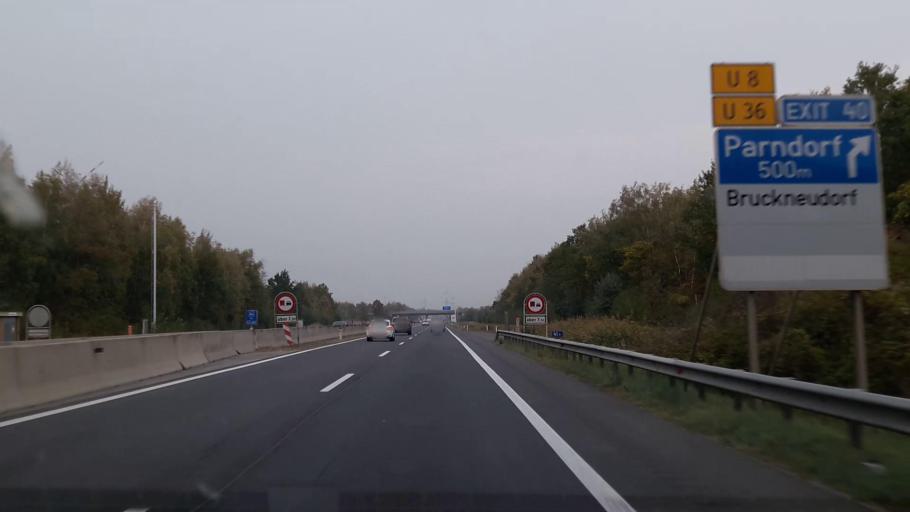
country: AT
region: Burgenland
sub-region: Politischer Bezirk Neusiedl am See
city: Parndorf
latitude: 47.9997
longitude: 16.8332
